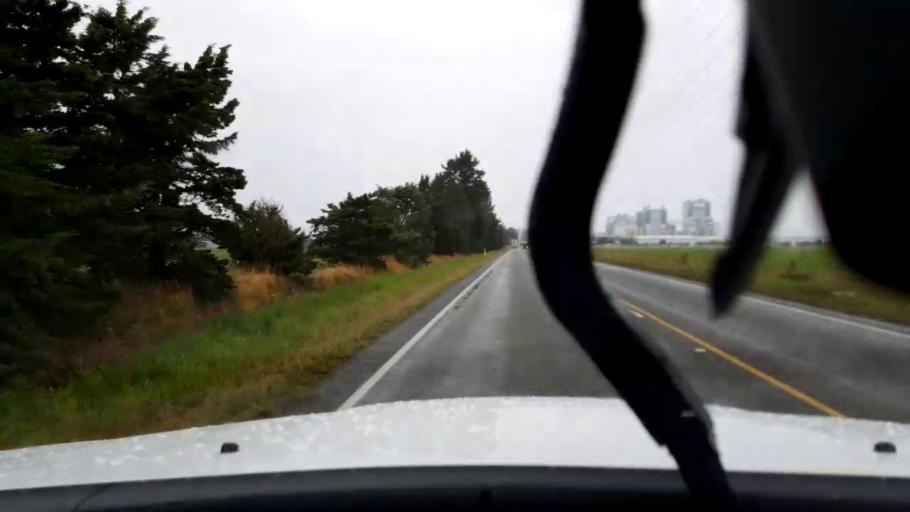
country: NZ
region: Canterbury
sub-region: Timaru District
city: Timaru
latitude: -44.2056
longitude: 171.3757
